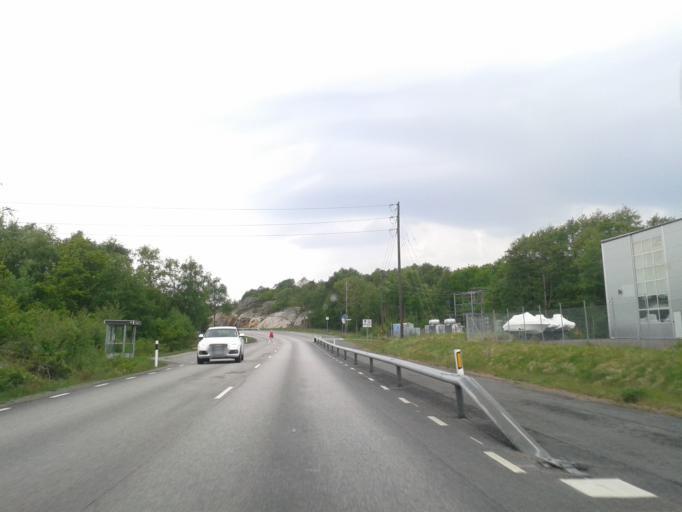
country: SE
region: Vaestra Goetaland
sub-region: Kungalvs Kommun
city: Marstrand
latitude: 57.8908
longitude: 11.6147
